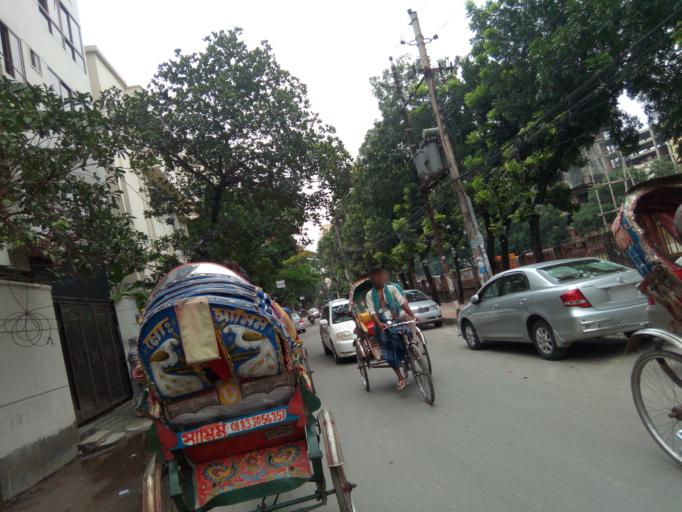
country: BD
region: Dhaka
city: Azimpur
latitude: 23.7580
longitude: 90.3727
